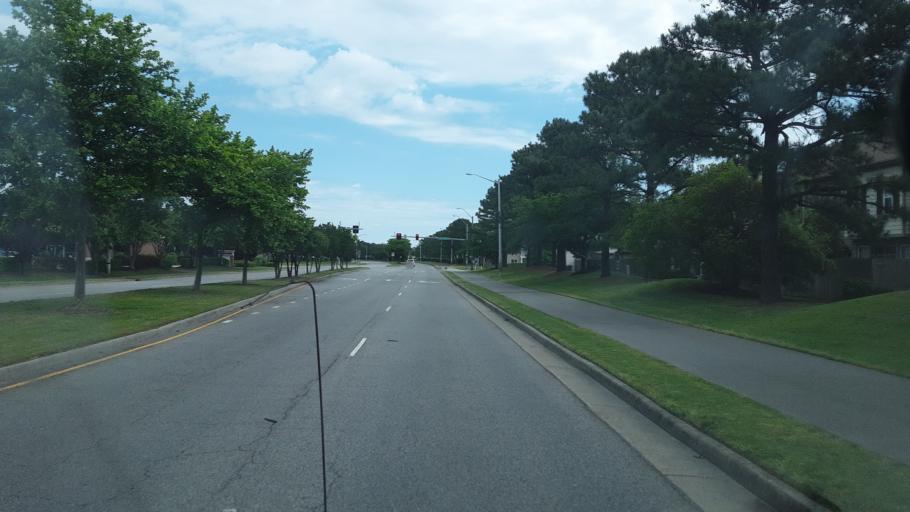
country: US
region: Virginia
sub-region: City of Virginia Beach
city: Virginia Beach
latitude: 36.7548
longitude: -76.0076
